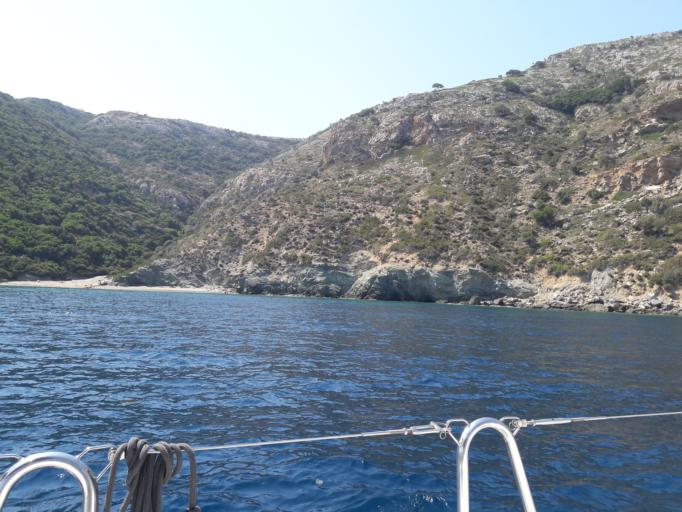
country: GR
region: Thessaly
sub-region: Nomos Magnisias
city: Patitirion
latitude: 39.3223
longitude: 24.0984
